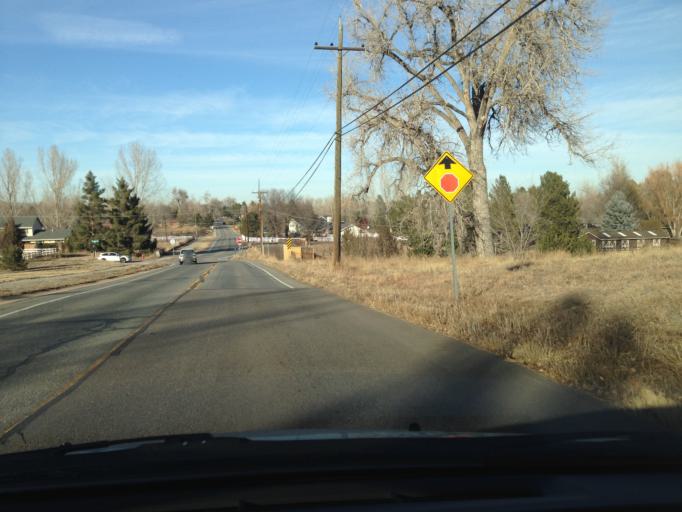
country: US
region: Colorado
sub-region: Boulder County
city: Niwot
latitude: 40.0934
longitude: -105.1690
